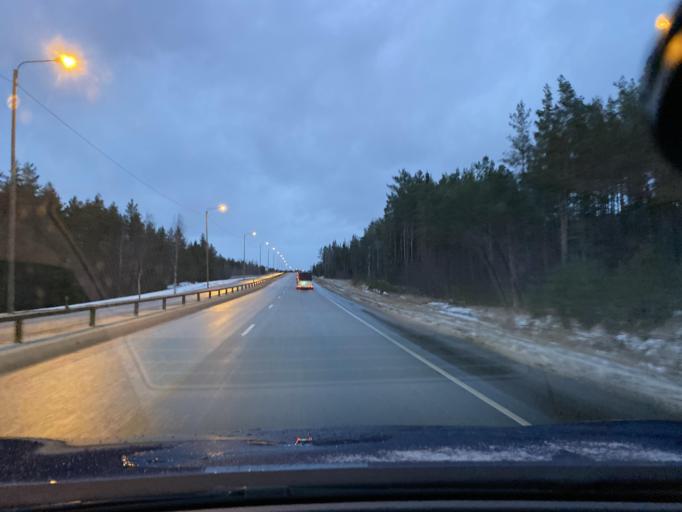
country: FI
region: Satakunta
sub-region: Rauma
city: Rauma
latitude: 61.1402
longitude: 21.5472
